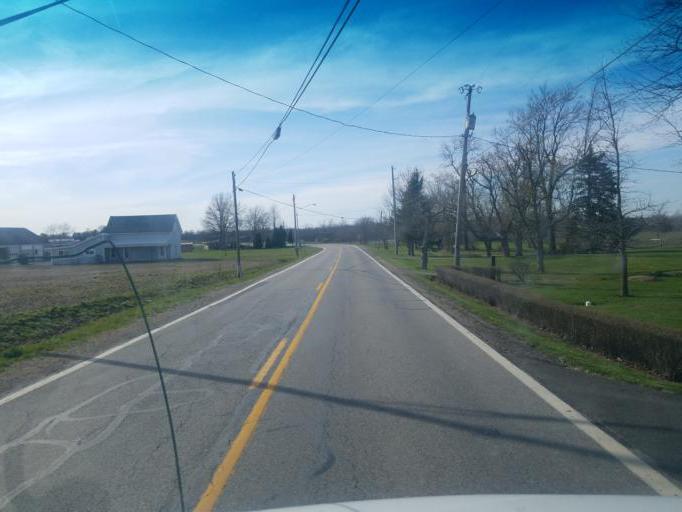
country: US
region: Ohio
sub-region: Champaign County
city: North Lewisburg
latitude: 40.3373
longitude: -83.4703
